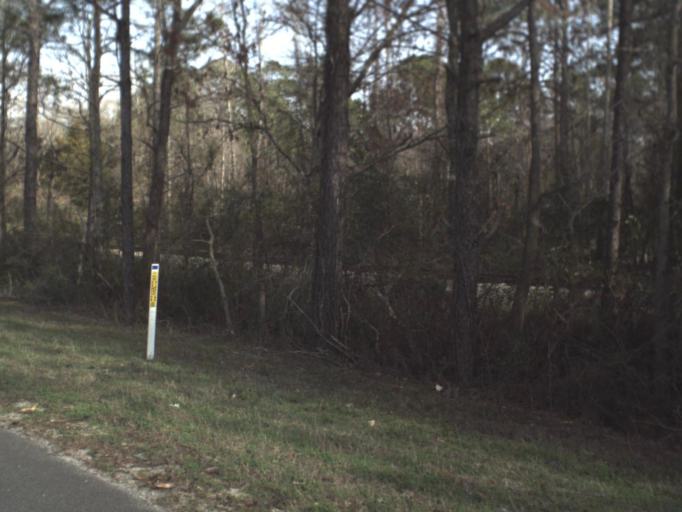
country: US
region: Florida
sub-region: Bay County
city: Hiland Park
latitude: 30.2165
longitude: -85.6025
